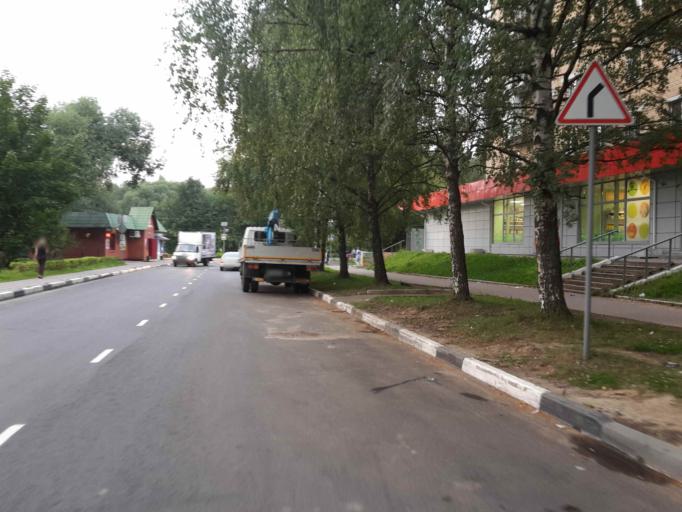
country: RU
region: Moskovskaya
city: Dolgoprudnyy
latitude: 55.9422
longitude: 37.5038
